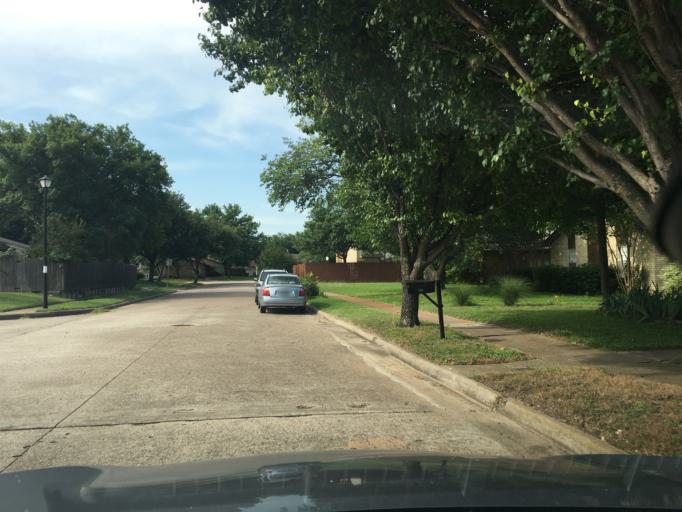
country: US
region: Texas
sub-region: Dallas County
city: Richardson
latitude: 32.9670
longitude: -96.6806
